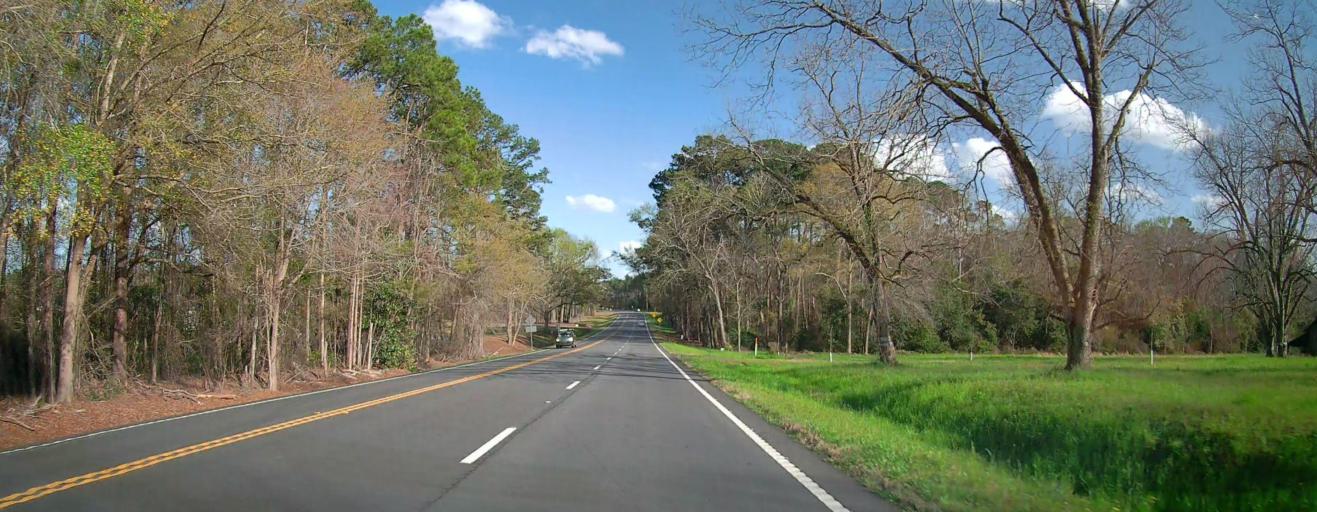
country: US
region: Georgia
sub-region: Montgomery County
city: Mount Vernon
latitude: 32.1818
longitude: -82.5602
